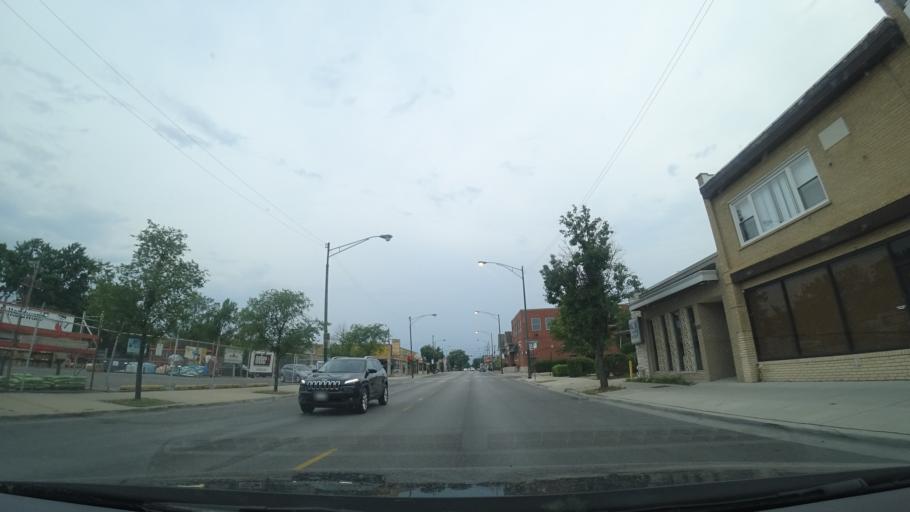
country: US
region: Illinois
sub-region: Cook County
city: Harwood Heights
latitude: 41.9591
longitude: -87.7672
